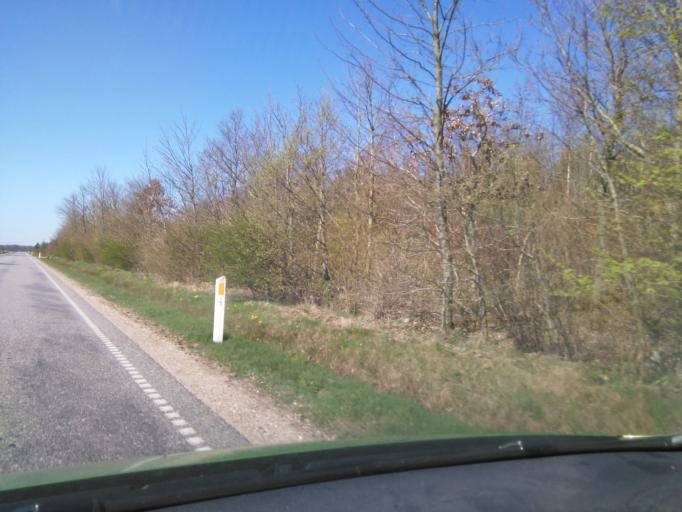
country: DK
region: South Denmark
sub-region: Billund Kommune
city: Grindsted
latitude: 55.7005
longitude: 8.8196
